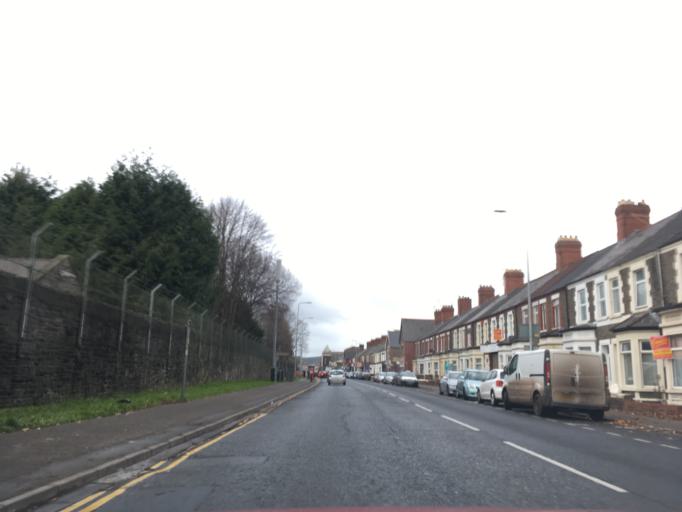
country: GB
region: Wales
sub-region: Cardiff
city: Cardiff
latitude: 51.4990
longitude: -3.1849
